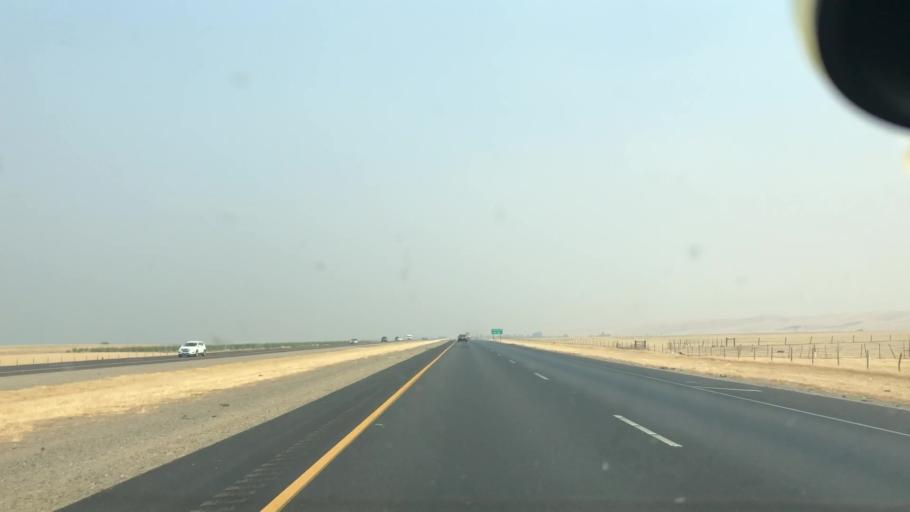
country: US
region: California
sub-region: San Joaquin County
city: Tracy
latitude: 37.6532
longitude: -121.4262
